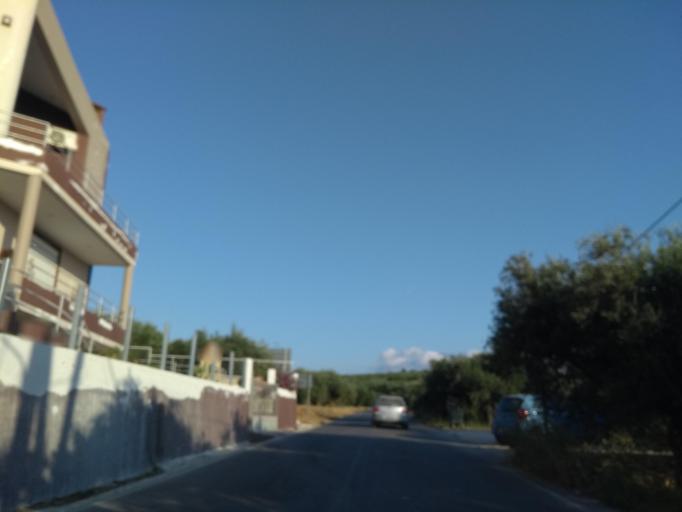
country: GR
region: Crete
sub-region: Nomos Chanias
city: Kalivai
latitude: 35.4482
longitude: 24.1753
